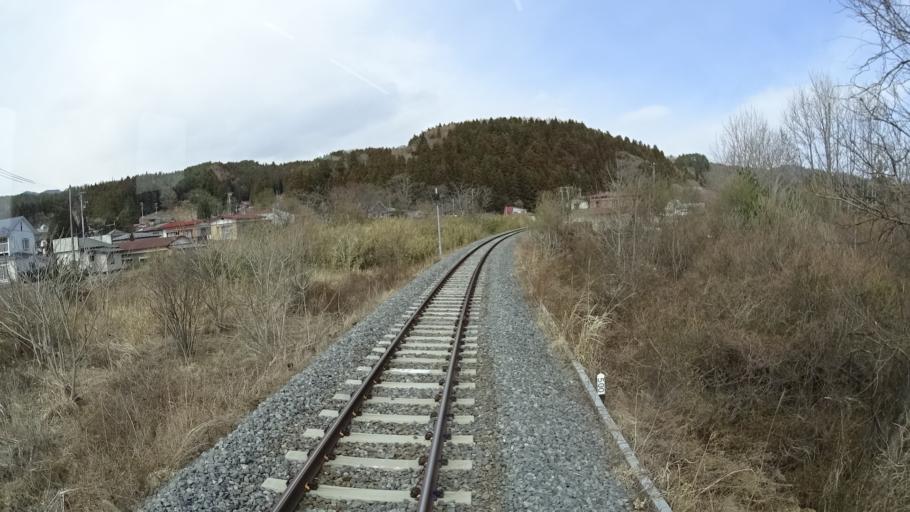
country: JP
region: Iwate
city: Miyako
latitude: 39.5649
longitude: 141.9324
